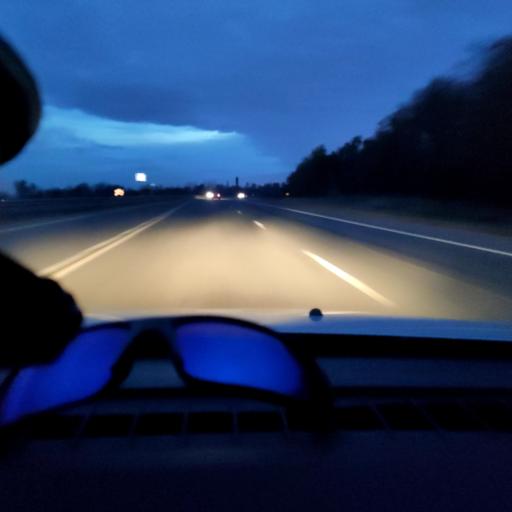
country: RU
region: Samara
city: Novokuybyshevsk
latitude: 53.0486
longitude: 50.0083
